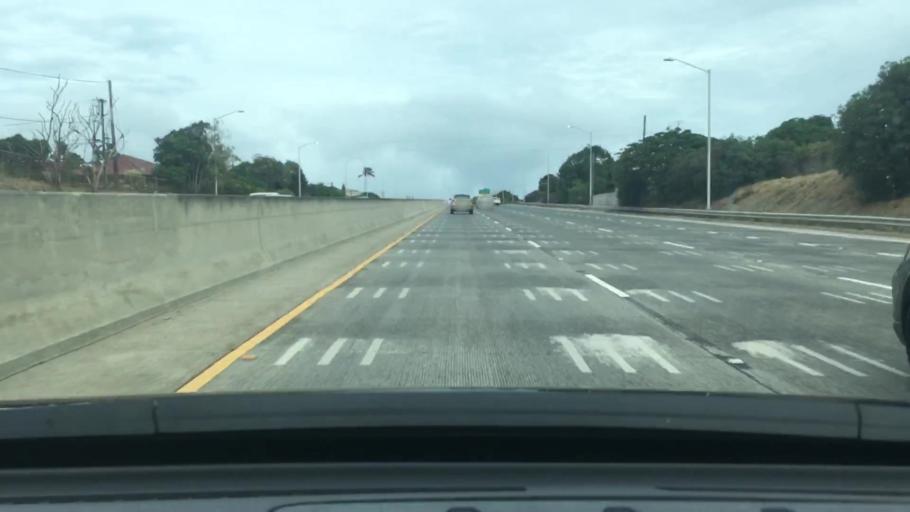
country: US
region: Hawaii
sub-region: Honolulu County
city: Honolulu
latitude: 21.2830
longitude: -157.8055
